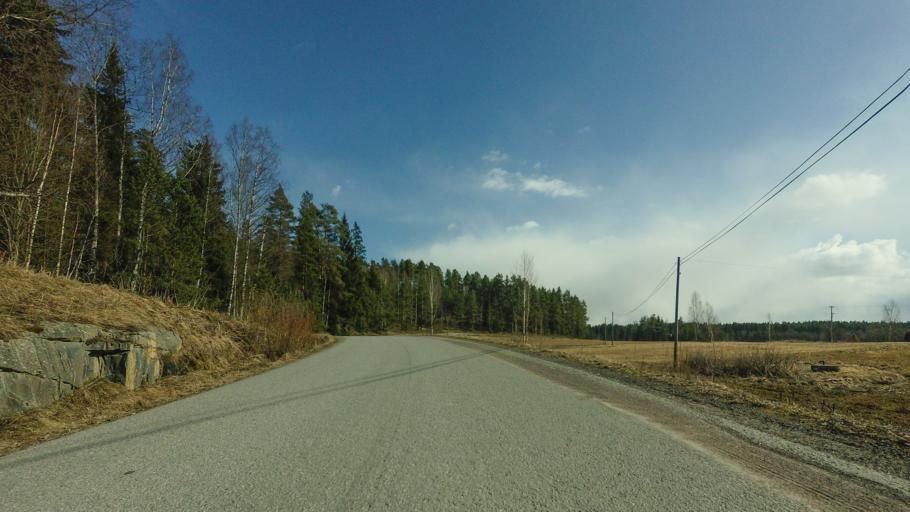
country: FI
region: Uusimaa
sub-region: Helsinki
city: Karjalohja
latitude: 60.2677
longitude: 23.6672
